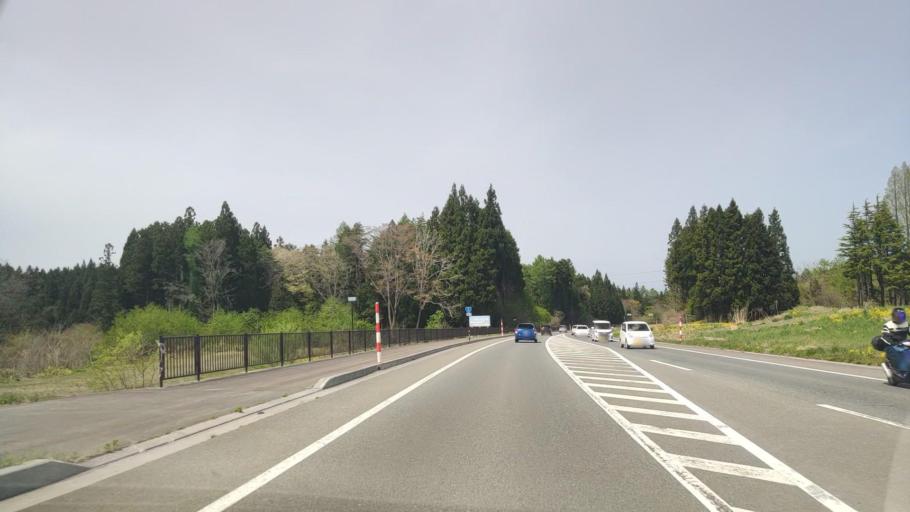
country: JP
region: Aomori
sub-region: Misawa Shi
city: Inuotose
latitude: 40.6782
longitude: 141.1728
